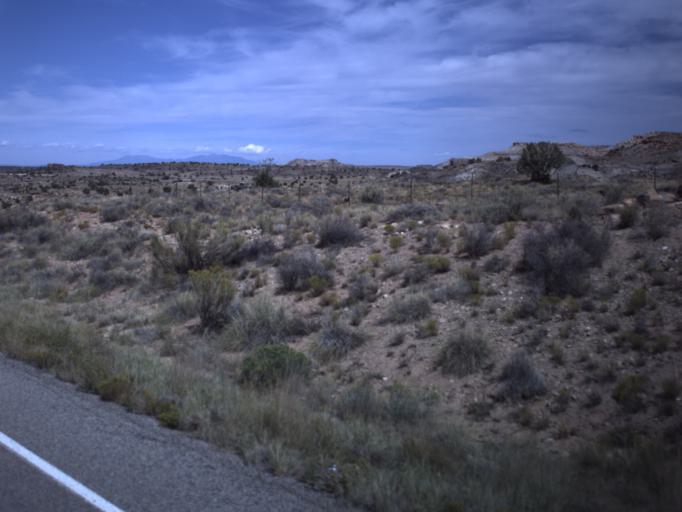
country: US
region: Colorado
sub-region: Montezuma County
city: Towaoc
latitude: 37.1787
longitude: -109.1233
